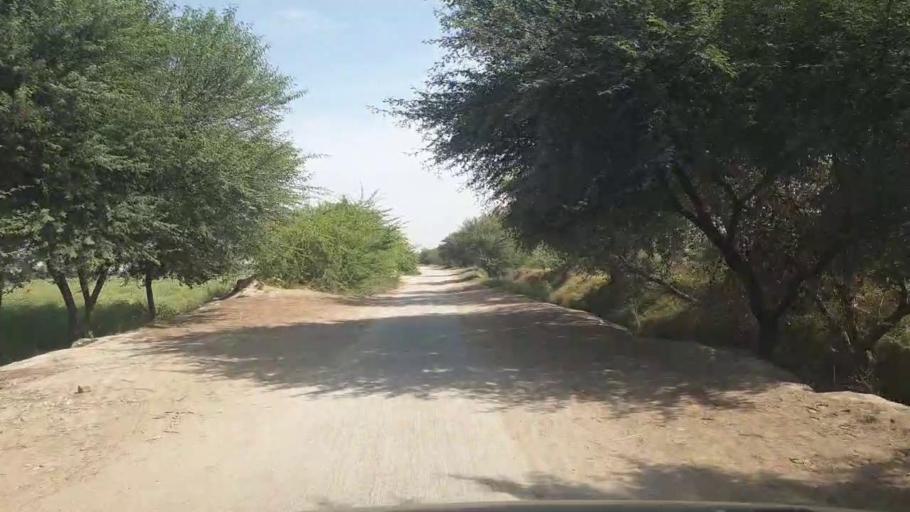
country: PK
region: Sindh
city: Kunri
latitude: 25.1923
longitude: 69.6789
